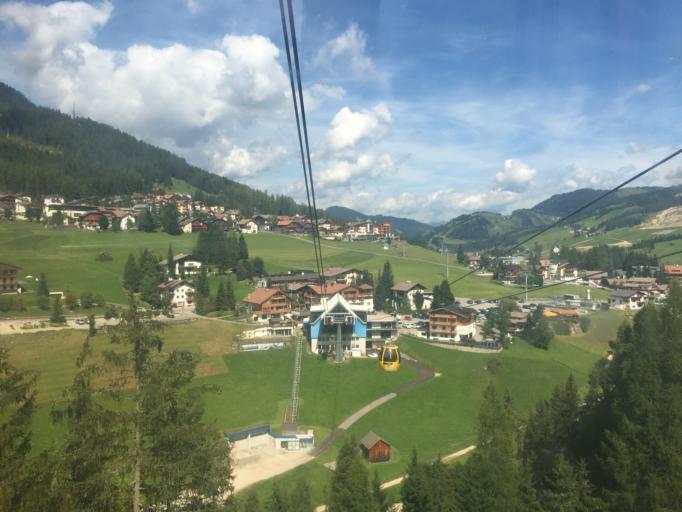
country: IT
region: Trentino-Alto Adige
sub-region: Bolzano
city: Badia
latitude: 46.5790
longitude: 11.9017
